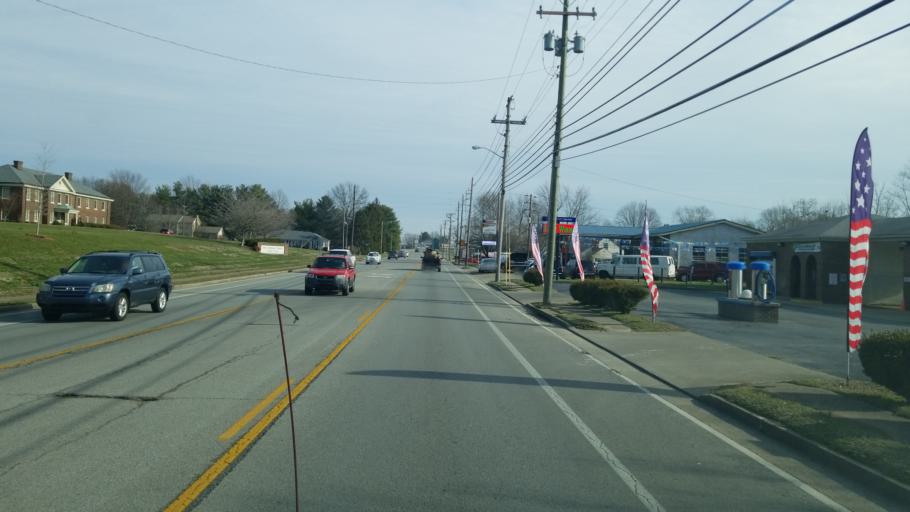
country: US
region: Kentucky
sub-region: Boyle County
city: Danville
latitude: 37.6534
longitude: -84.7564
